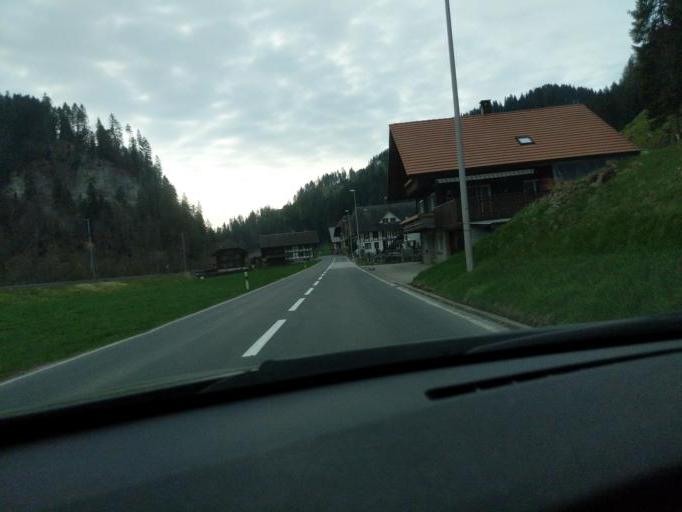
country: CH
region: Bern
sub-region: Emmental District
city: Trub
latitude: 46.9132
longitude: 7.8739
